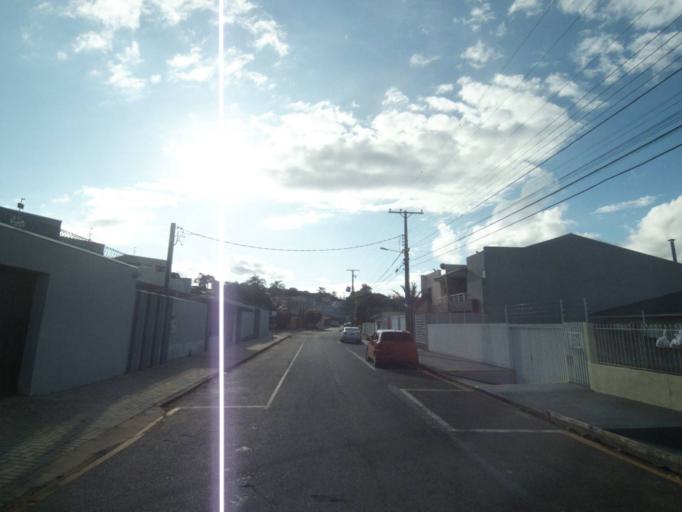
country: BR
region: Parana
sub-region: Telemaco Borba
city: Telemaco Borba
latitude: -24.3352
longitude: -50.6232
